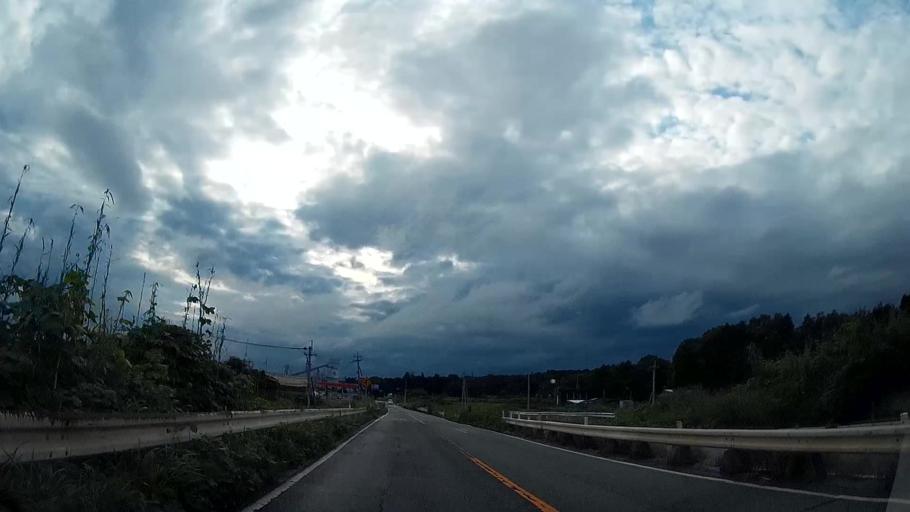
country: JP
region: Kumamoto
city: Ozu
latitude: 32.8784
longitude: 130.9148
